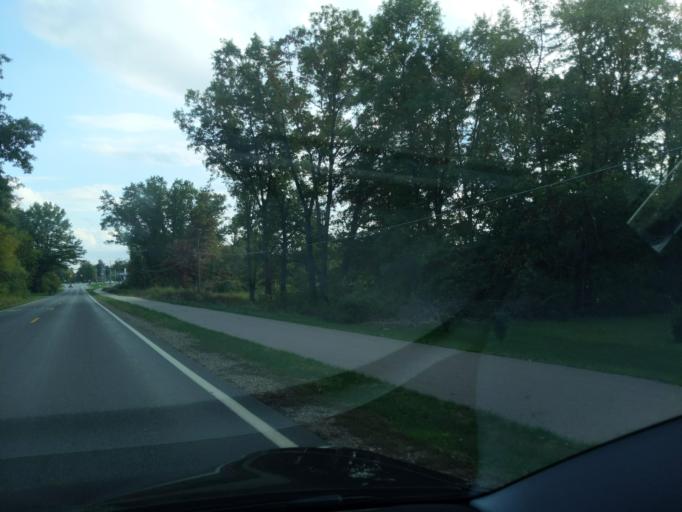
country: US
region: Michigan
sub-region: Jackson County
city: Jackson
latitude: 42.3259
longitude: -84.4629
